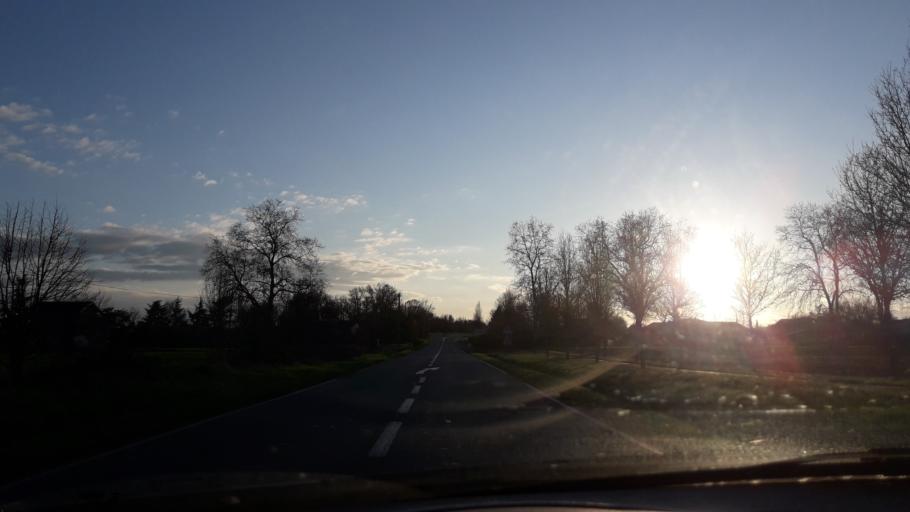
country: FR
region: Midi-Pyrenees
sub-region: Departement de la Haute-Garonne
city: Levignac
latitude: 43.6401
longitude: 1.1565
